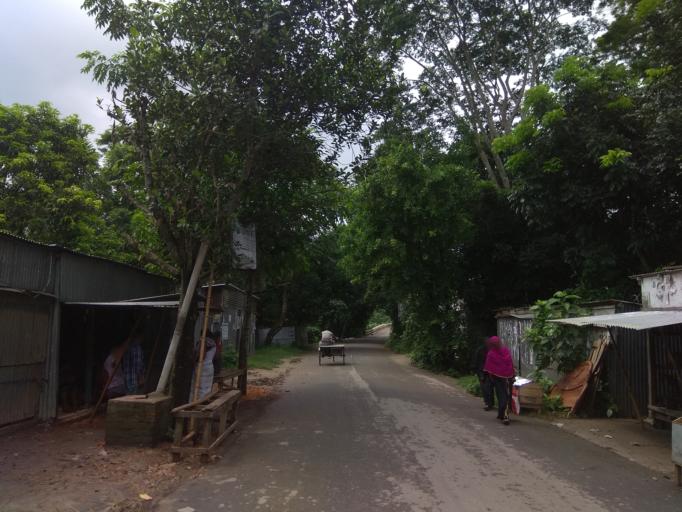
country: BD
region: Dhaka
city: Dohar
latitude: 23.4429
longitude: 90.0709
